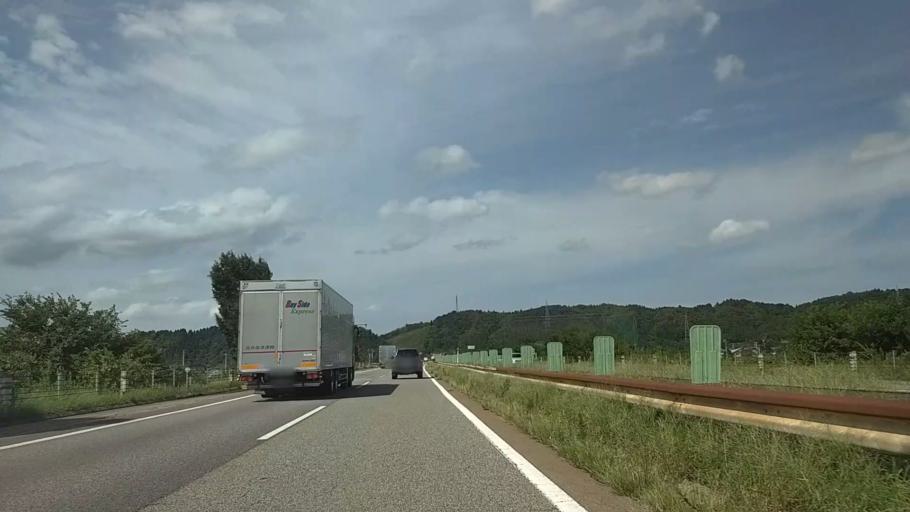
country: JP
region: Toyama
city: Toyama-shi
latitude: 36.6768
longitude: 137.1621
